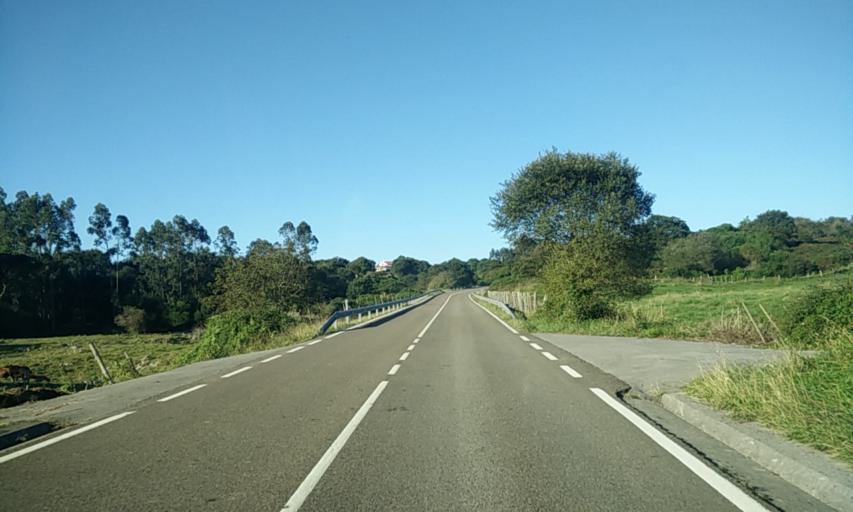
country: ES
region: Cantabria
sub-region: Provincia de Cantabria
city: San Vicente de la Barquera
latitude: 43.3819
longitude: -4.3460
